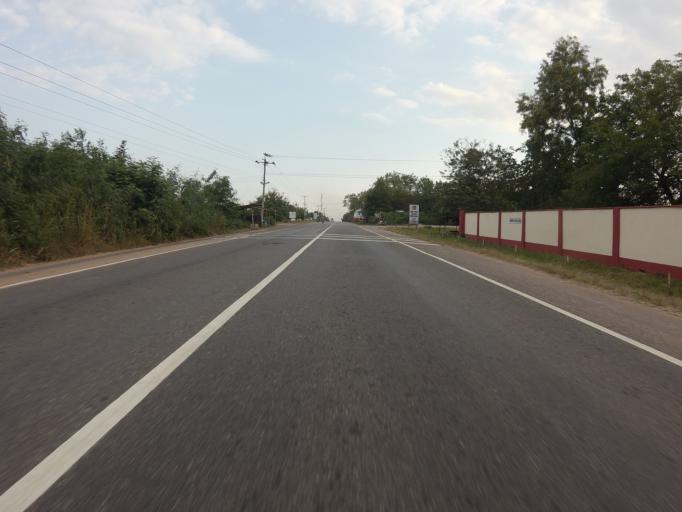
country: GH
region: Volta
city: Anloga
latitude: 6.0927
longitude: 0.5077
